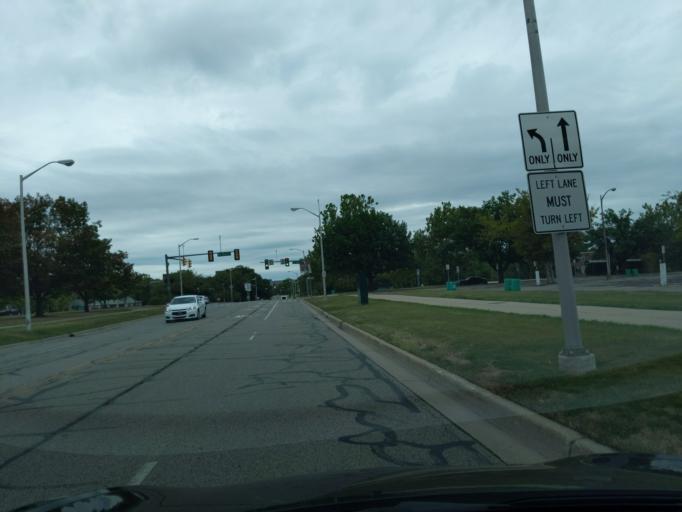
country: US
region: Michigan
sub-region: Ingham County
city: East Lansing
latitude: 42.7253
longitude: -84.4779
